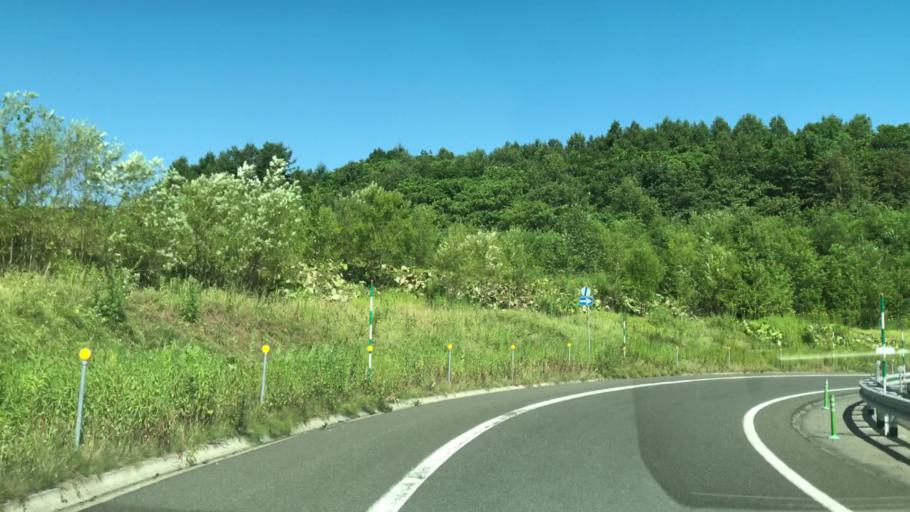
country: JP
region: Hokkaido
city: Shimo-furano
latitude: 42.9793
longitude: 142.4078
